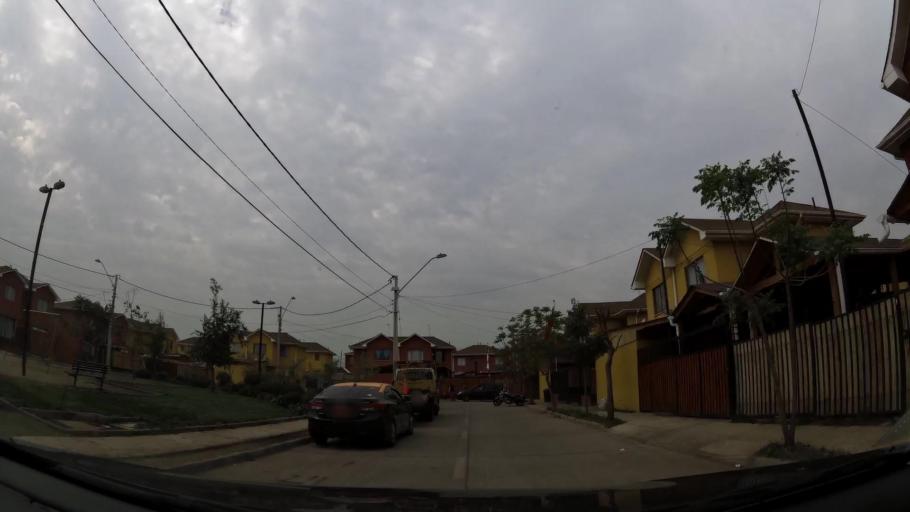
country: CL
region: Santiago Metropolitan
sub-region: Provincia de Chacabuco
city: Chicureo Abajo
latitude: -33.1928
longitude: -70.6795
